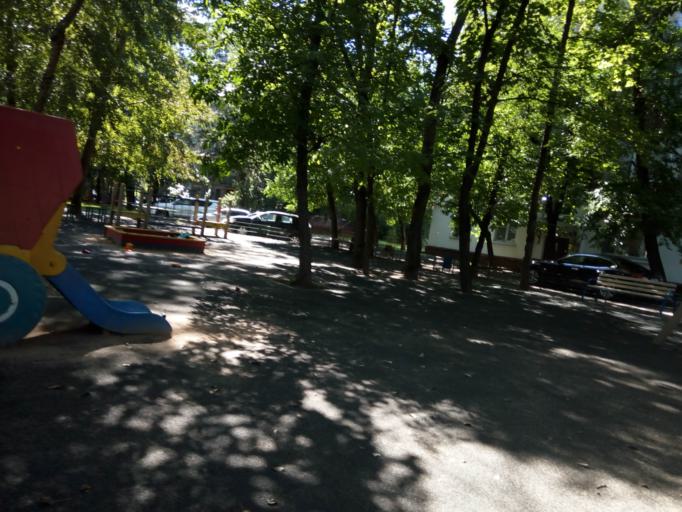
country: RU
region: Moskovskaya
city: Presnenskiy
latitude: 55.7737
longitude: 37.5334
